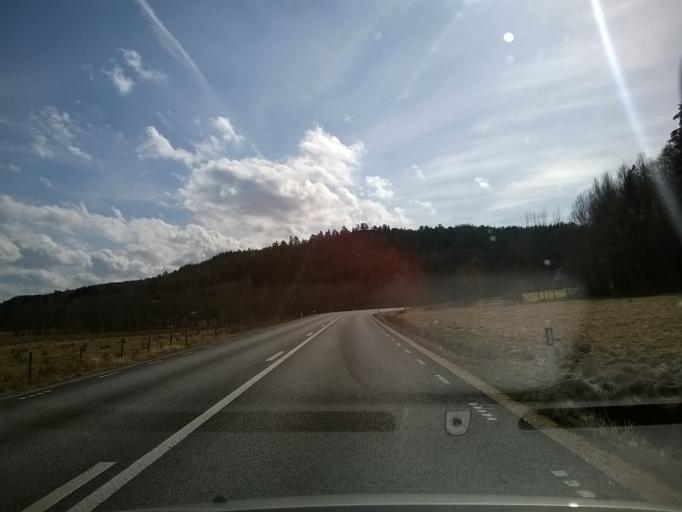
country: SE
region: Vaestra Goetaland
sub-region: Orust
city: Henan
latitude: 58.3382
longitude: 11.6927
